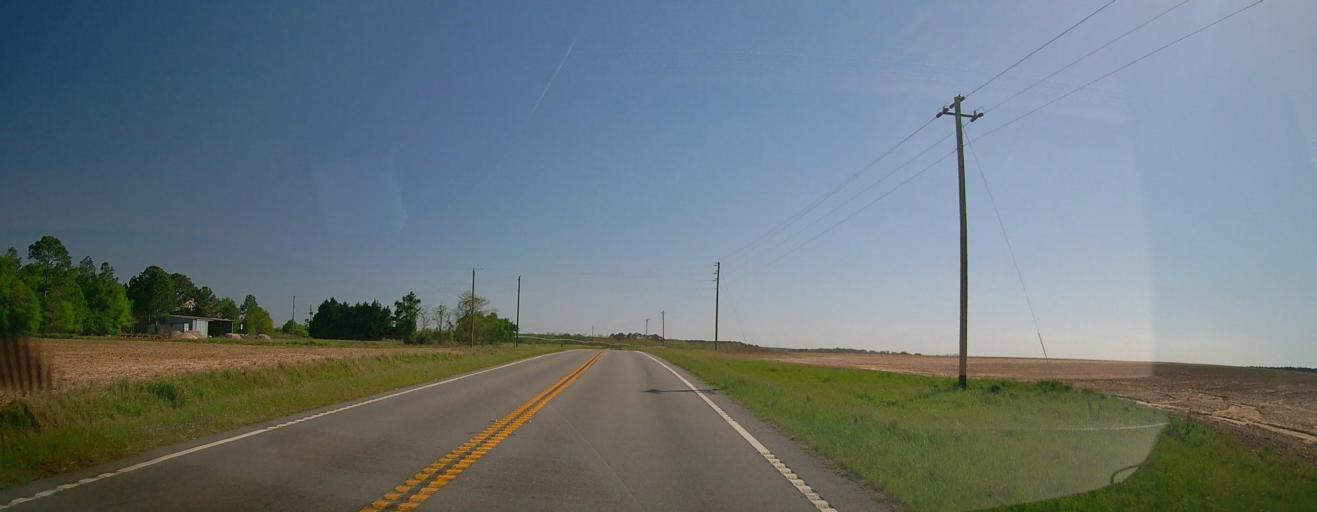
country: US
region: Georgia
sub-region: Pulaski County
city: Hawkinsville
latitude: 32.1840
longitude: -83.5043
